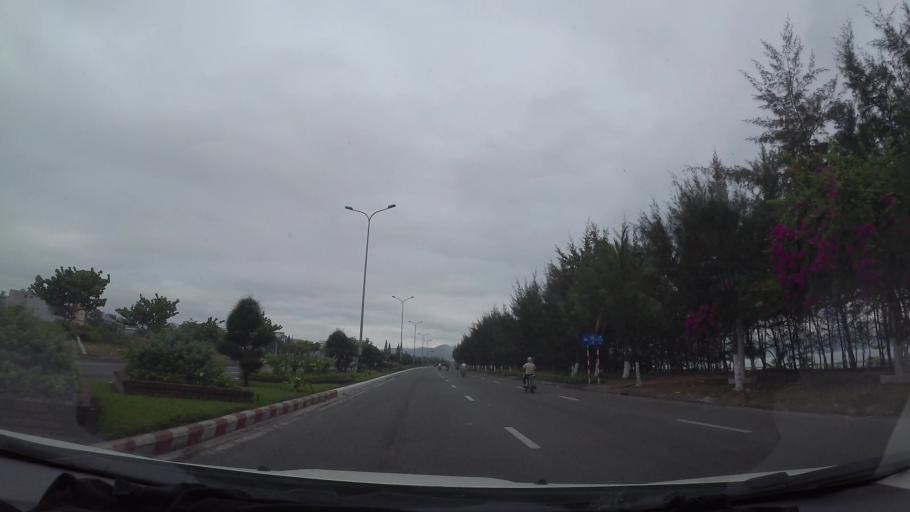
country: VN
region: Da Nang
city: Lien Chieu
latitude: 16.0909
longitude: 108.1512
